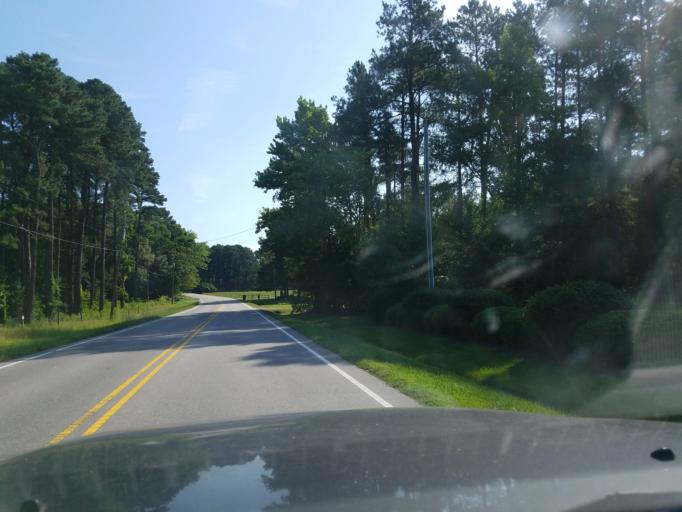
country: US
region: North Carolina
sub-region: Granville County
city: Butner
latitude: 36.1731
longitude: -78.7563
